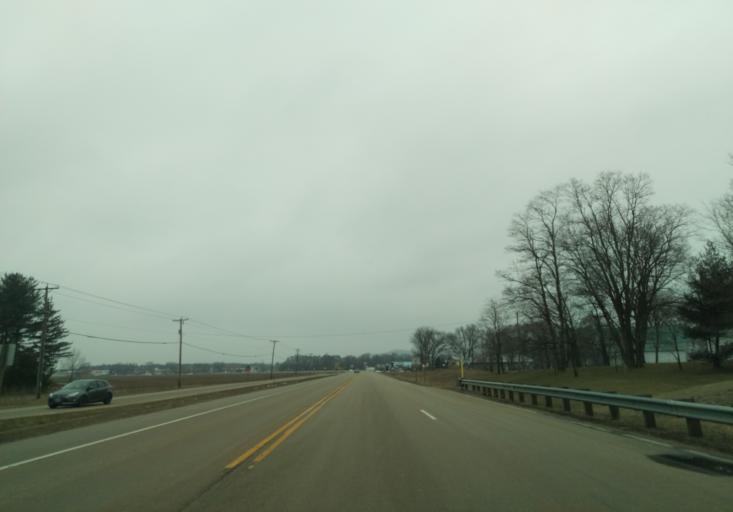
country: US
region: Wisconsin
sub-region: Sauk County
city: Spring Green
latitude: 43.1857
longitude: -90.0641
